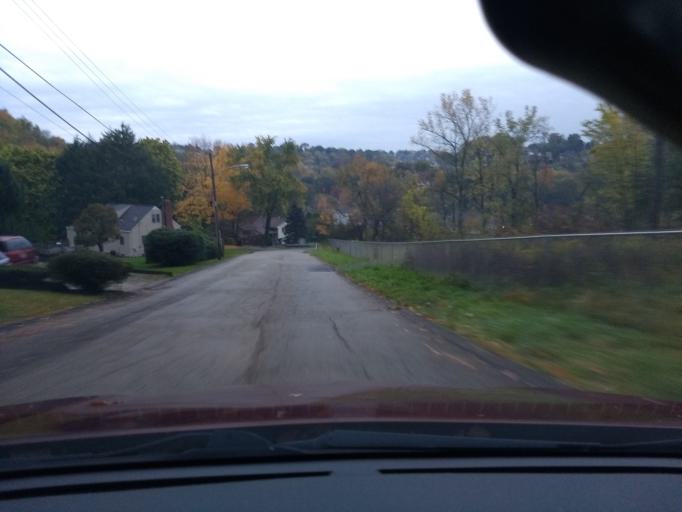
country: US
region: Pennsylvania
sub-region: Allegheny County
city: Pleasant Hills
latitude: 40.3502
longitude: -79.9590
